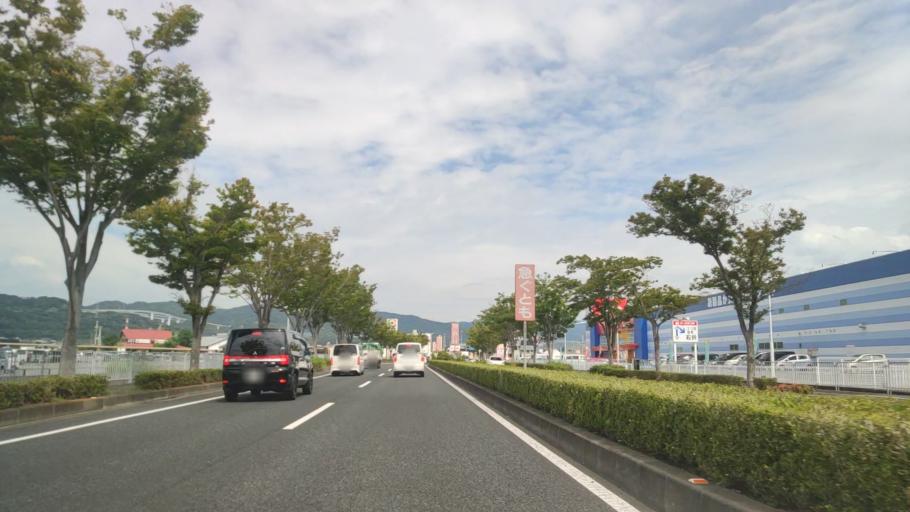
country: JP
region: Wakayama
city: Iwade
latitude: 34.2607
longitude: 135.2648
